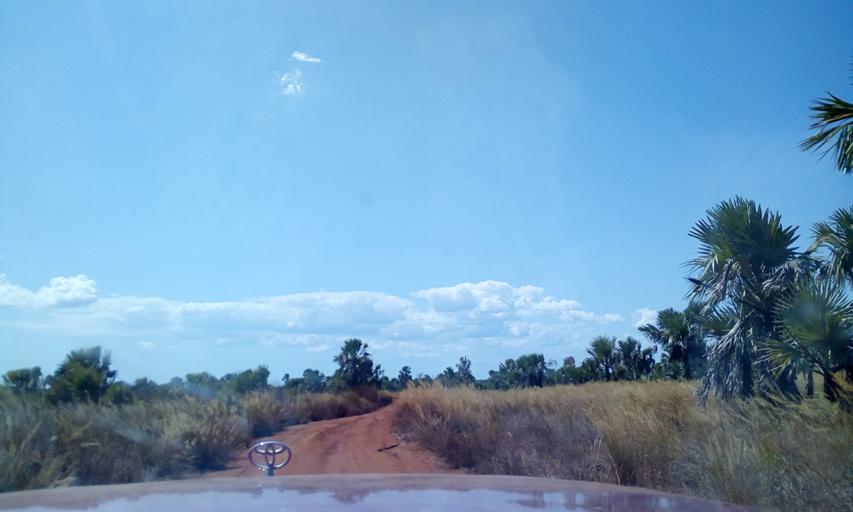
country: MG
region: Boeny
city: Sitampiky
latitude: -16.1237
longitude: 45.4564
